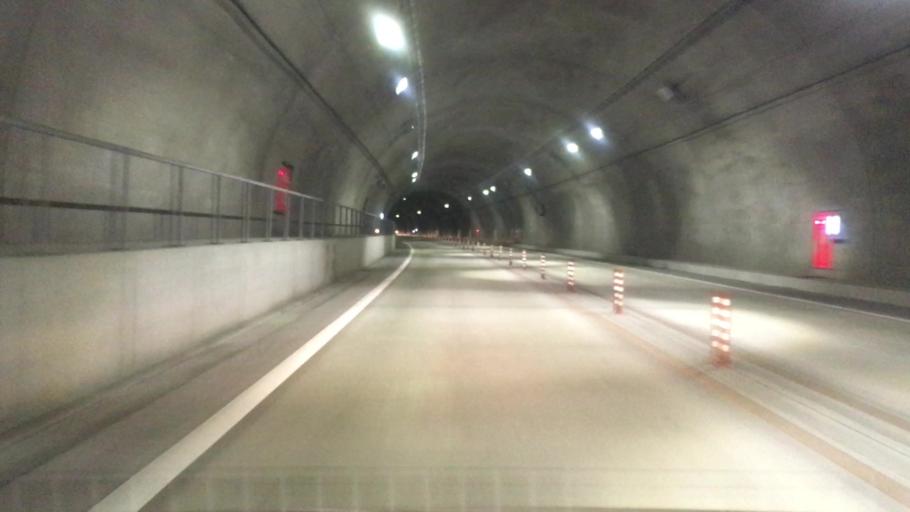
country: JP
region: Hyogo
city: Toyooka
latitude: 35.6406
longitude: 134.5480
